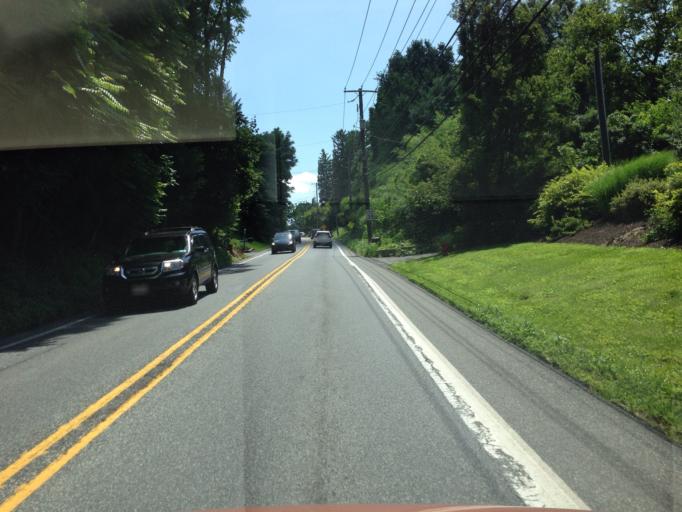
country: US
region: Pennsylvania
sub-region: Lancaster County
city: East Petersburg
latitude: 40.0931
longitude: -76.3296
